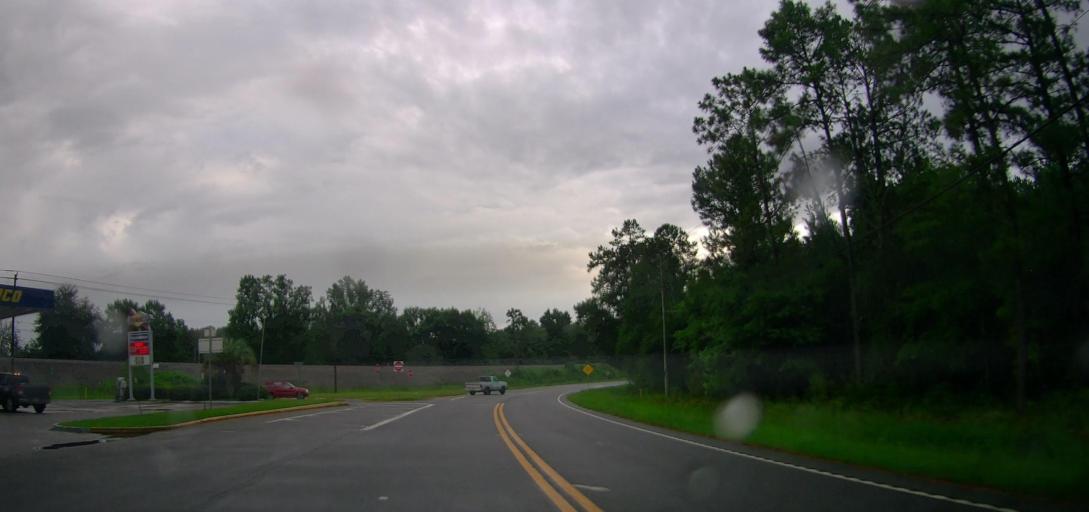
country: US
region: Georgia
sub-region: Ware County
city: Deenwood
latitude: 31.2594
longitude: -82.3797
